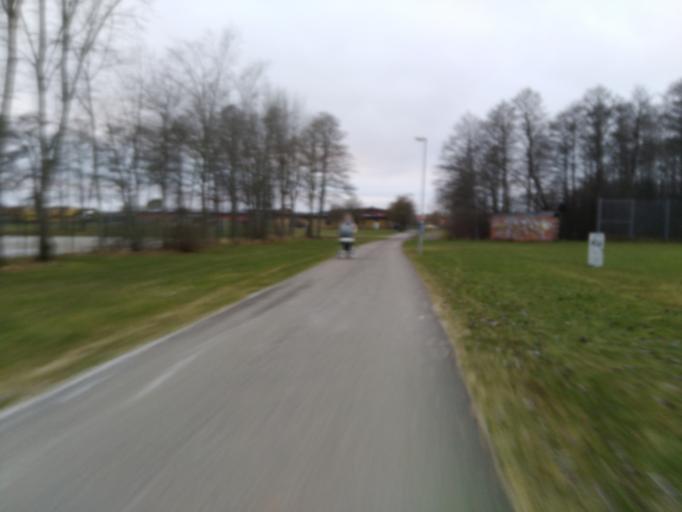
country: SE
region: Vaestra Goetaland
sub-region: Lidkopings Kommun
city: Lidkoping
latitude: 58.4928
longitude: 13.1767
